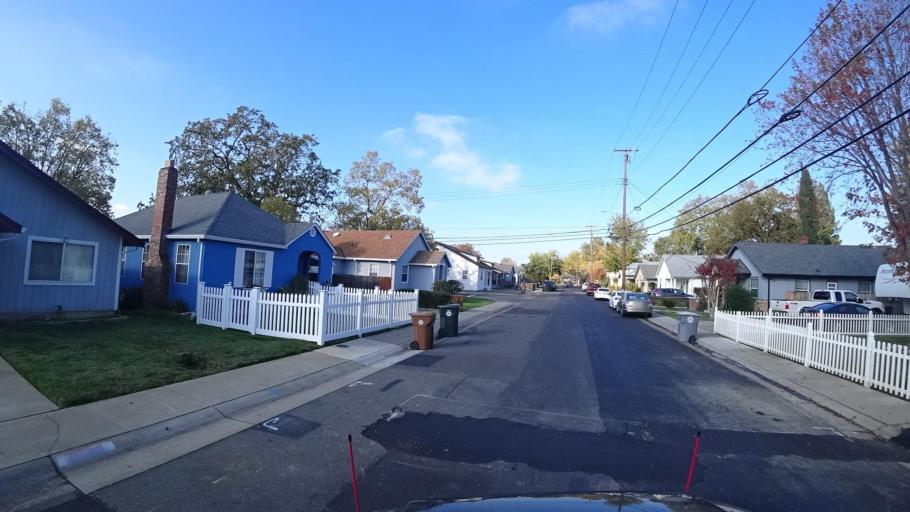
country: US
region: California
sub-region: Sacramento County
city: Elk Grove
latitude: 38.4097
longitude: -121.3670
